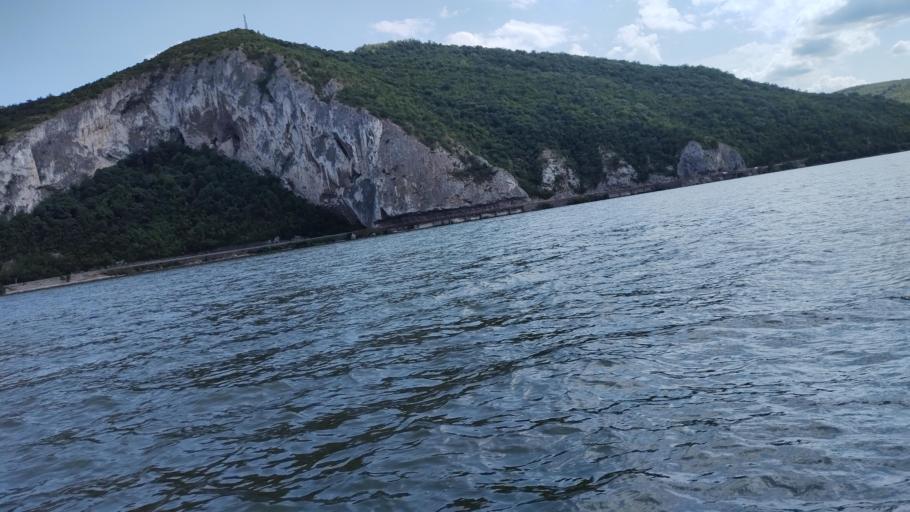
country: RO
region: Caras-Severin
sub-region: Comuna Pescari
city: Coronini
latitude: 44.6630
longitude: 21.6667
